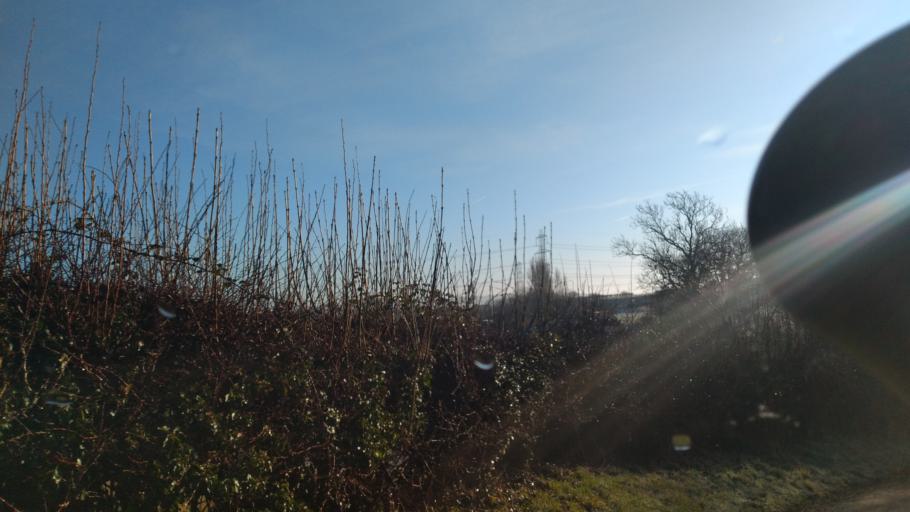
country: GB
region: England
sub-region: Wiltshire
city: Lacock
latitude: 51.4213
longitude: -2.1482
